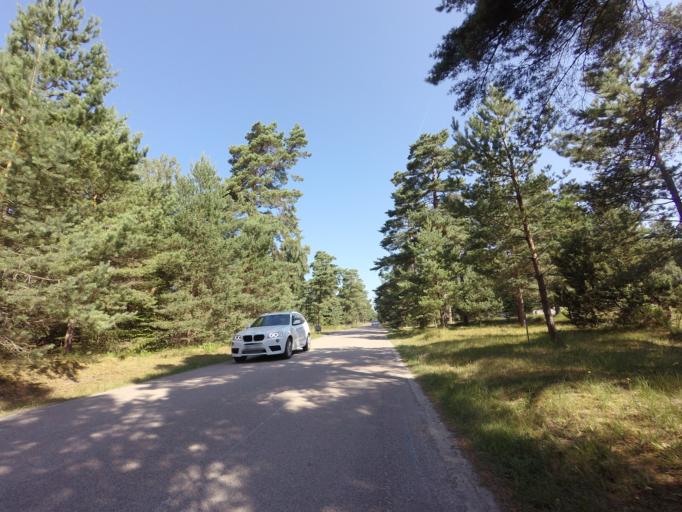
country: SE
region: Skane
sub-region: Vellinge Kommun
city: Ljunghusen
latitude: 55.3949
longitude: 12.9236
